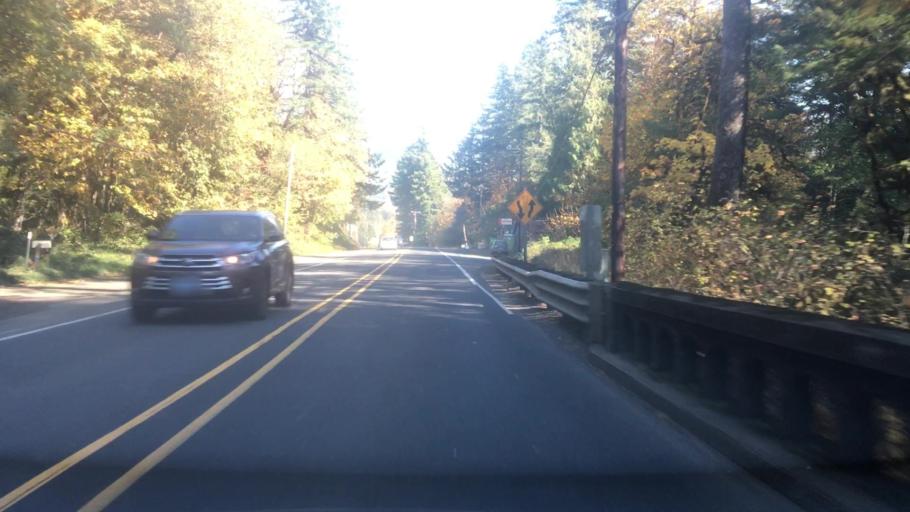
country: US
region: Oregon
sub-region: Lincoln County
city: Rose Lodge
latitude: 45.0192
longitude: -123.8666
